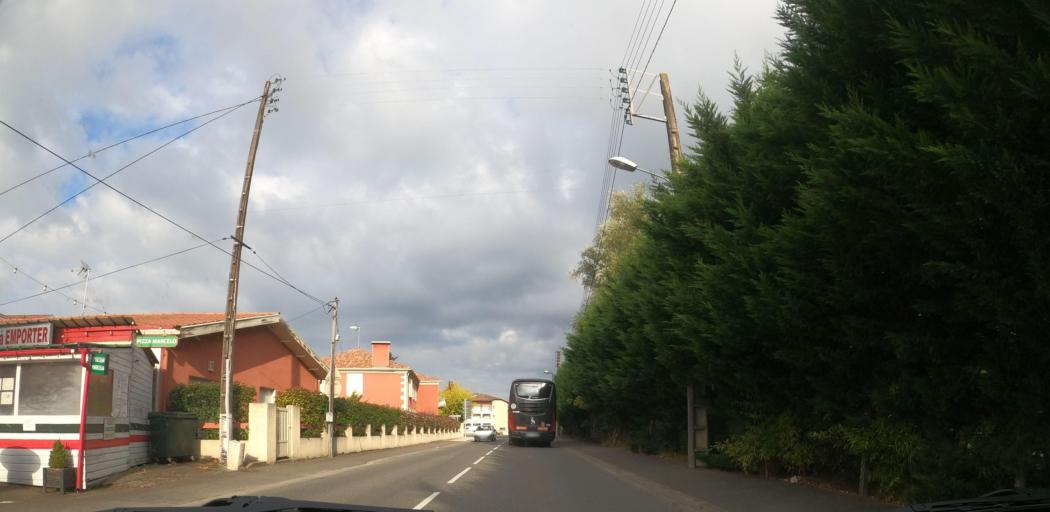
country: FR
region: Aquitaine
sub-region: Departement des Landes
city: Soustons
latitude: 43.7528
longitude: -1.3246
